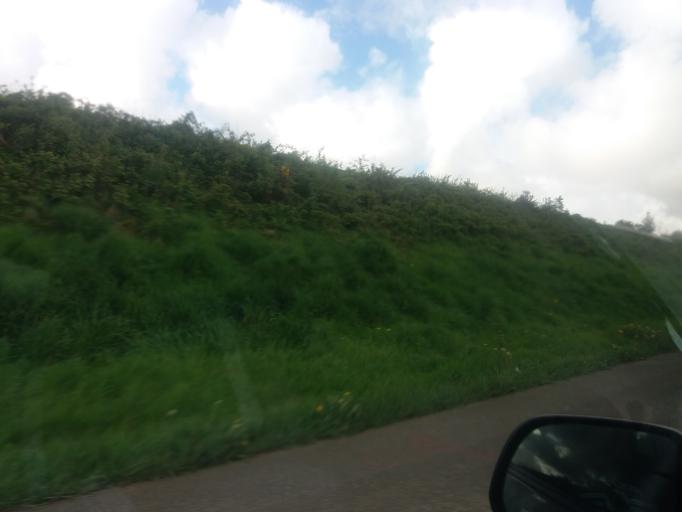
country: IE
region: Leinster
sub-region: Loch Garman
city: Gorey
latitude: 52.6338
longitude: -6.3634
